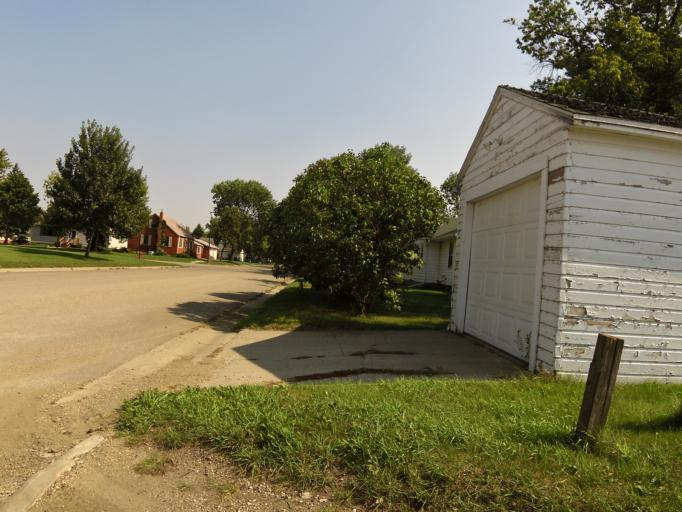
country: US
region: North Dakota
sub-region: Walsh County
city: Grafton
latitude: 48.4154
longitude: -97.4063
